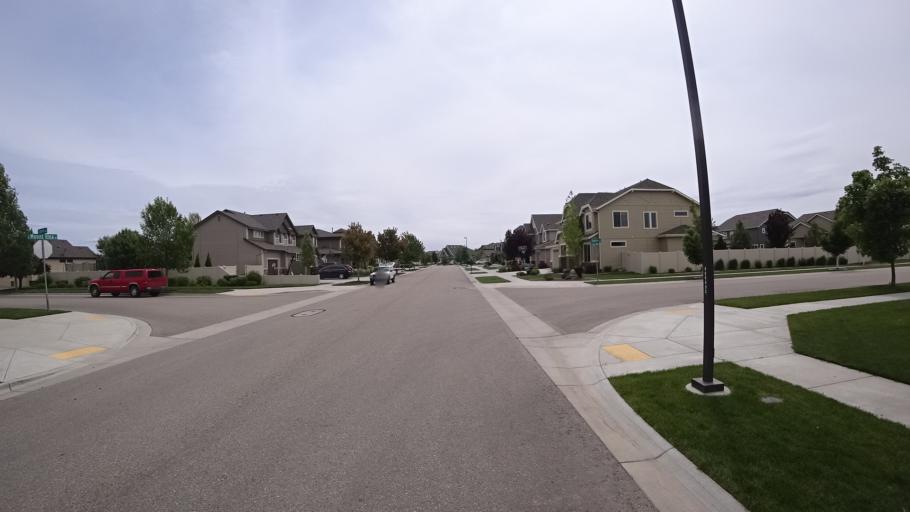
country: US
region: Idaho
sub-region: Ada County
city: Meridian
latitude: 43.5642
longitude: -116.3634
